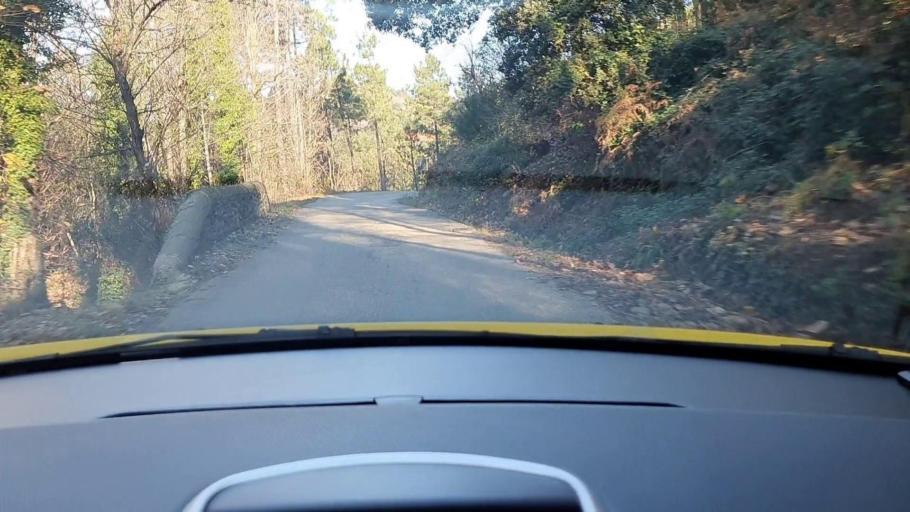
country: FR
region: Languedoc-Roussillon
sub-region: Departement du Gard
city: Branoux-les-Taillades
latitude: 44.2575
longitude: 3.9773
